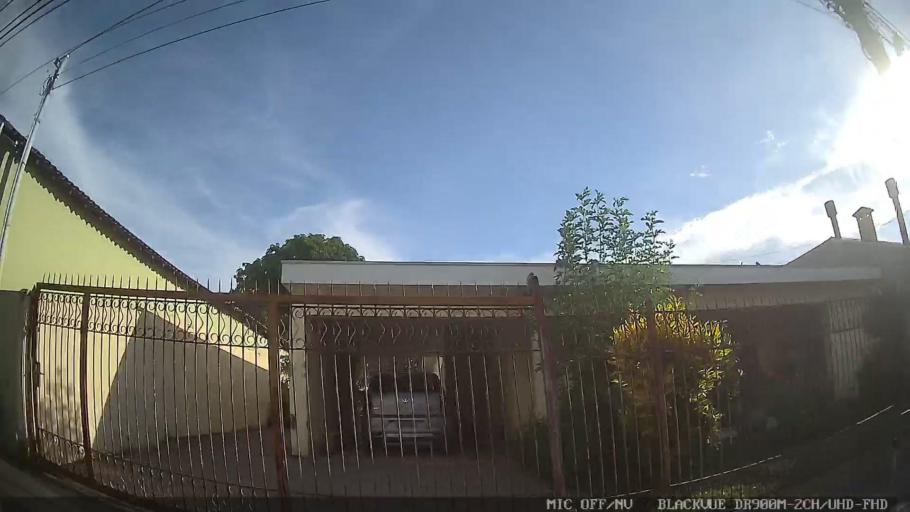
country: BR
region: Sao Paulo
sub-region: Tiete
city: Tiete
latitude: -23.1122
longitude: -47.7114
